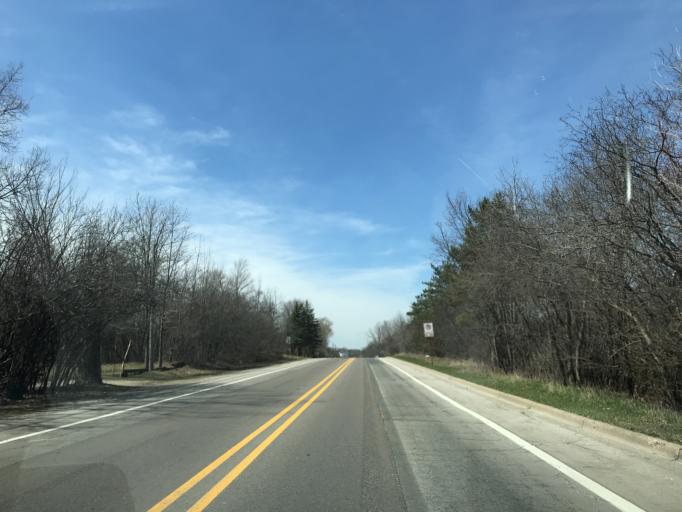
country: US
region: Michigan
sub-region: Washtenaw County
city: Ann Arbor
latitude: 42.2570
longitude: -83.7524
